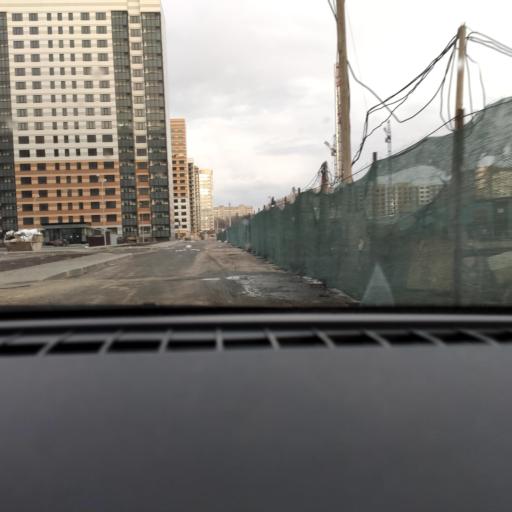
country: RU
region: Voronezj
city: Voronezh
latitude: 51.7122
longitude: 39.2643
